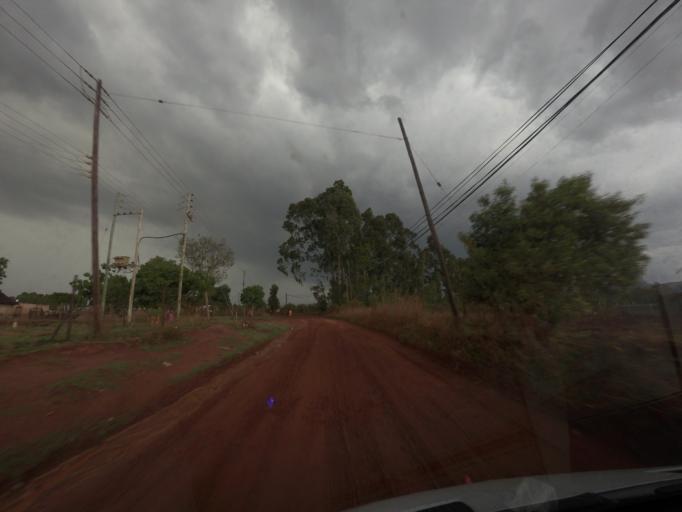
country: SZ
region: Hhohho
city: Lobamba
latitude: -26.4682
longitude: 31.2091
